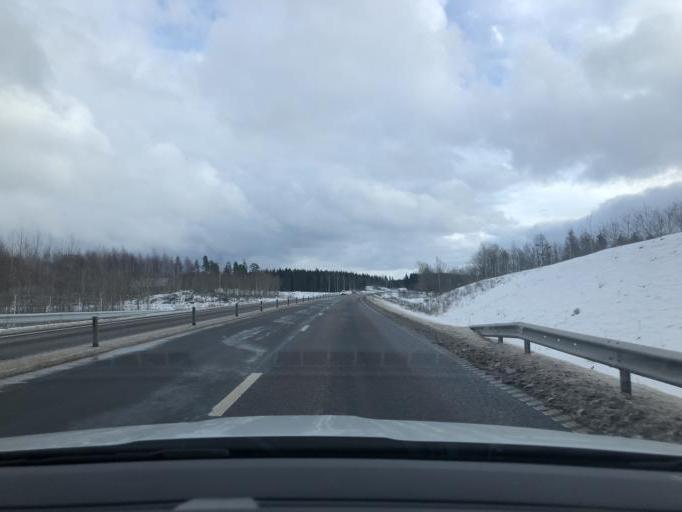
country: SE
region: OEstergoetland
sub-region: Motala Kommun
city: Borensberg
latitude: 58.5891
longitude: 15.1800
